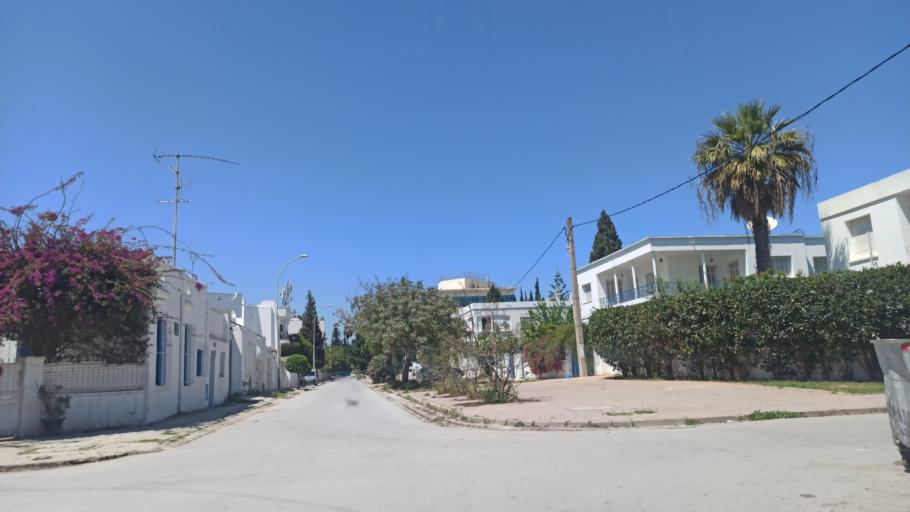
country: TN
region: Tunis
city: Tunis
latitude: 36.8239
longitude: 10.1844
